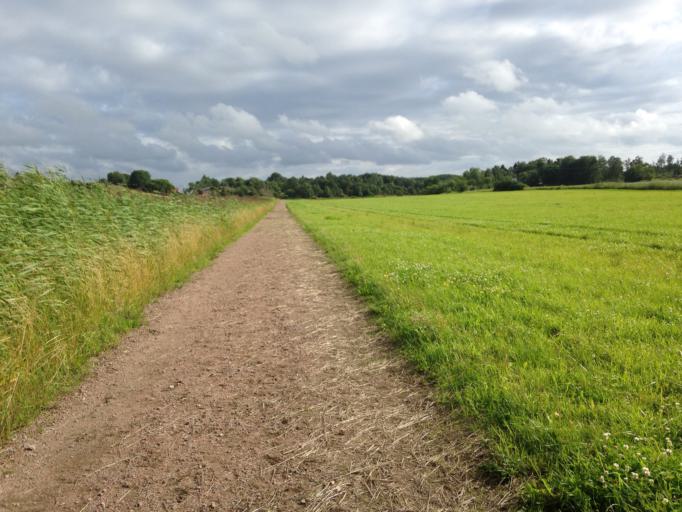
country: SE
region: Vaestra Goetaland
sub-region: Kungalvs Kommun
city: Kungalv
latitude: 57.8067
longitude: 11.8854
